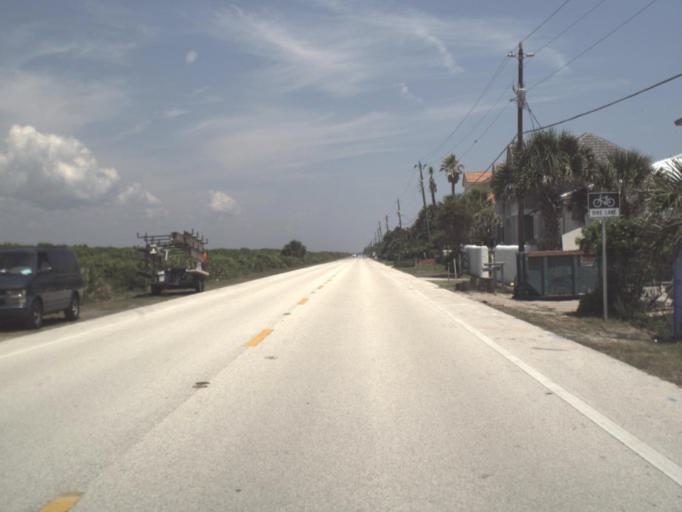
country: US
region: Florida
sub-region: Saint Johns County
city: Villano Beach
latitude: 30.0302
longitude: -81.3252
